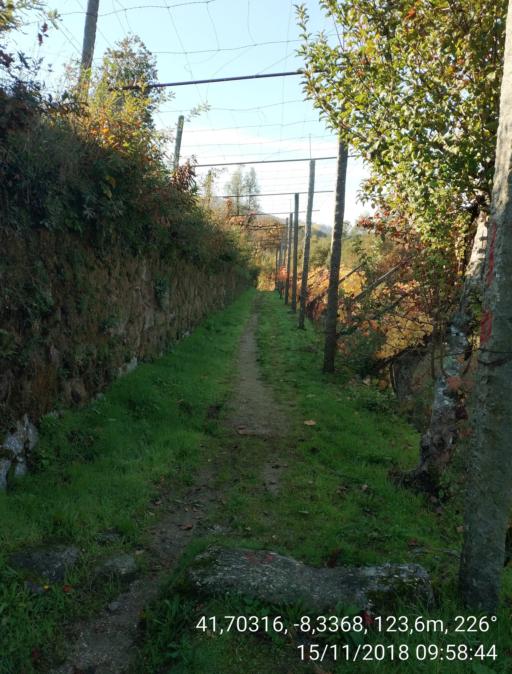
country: PT
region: Braga
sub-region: Terras de Bouro
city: Terras de Bouro
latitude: 41.7031
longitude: -8.3368
